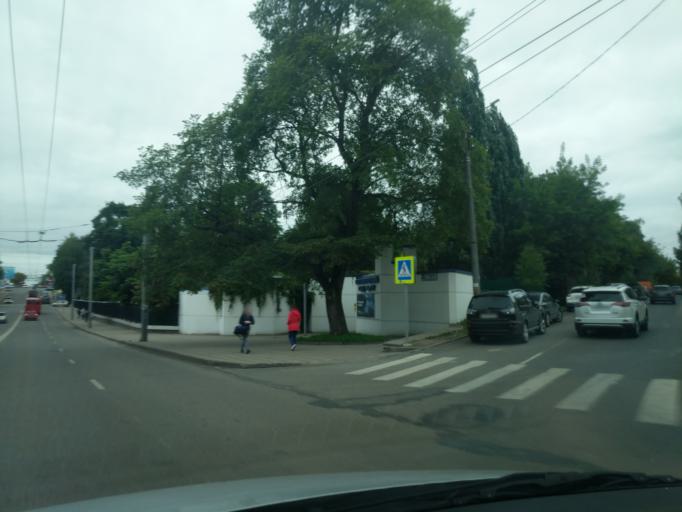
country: RU
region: Kirov
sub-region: Kirovo-Chepetskiy Rayon
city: Kirov
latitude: 58.5974
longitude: 49.6684
